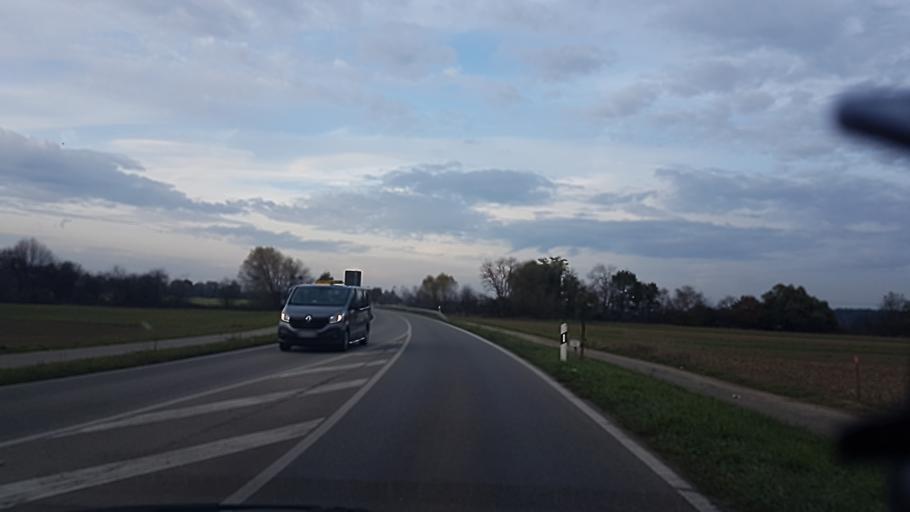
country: DE
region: Baden-Wuerttemberg
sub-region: Freiburg Region
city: Rust
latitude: 48.2440
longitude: 7.7155
